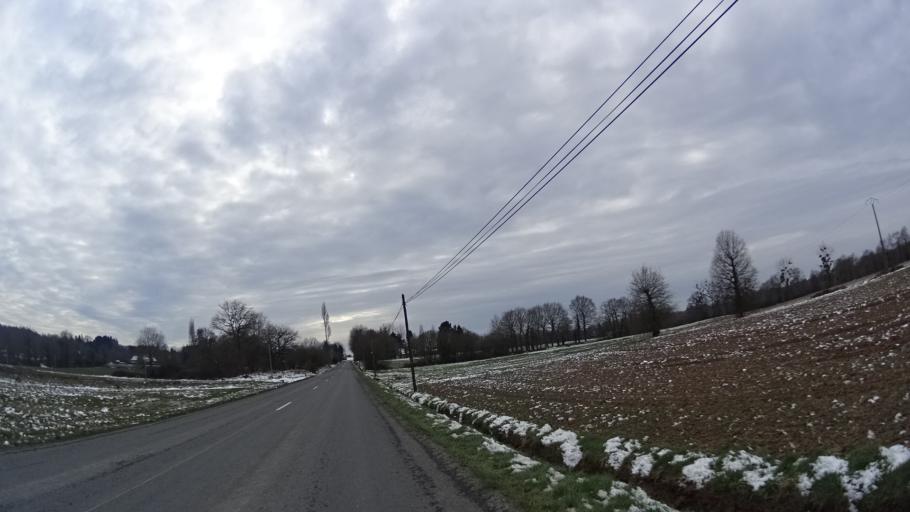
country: FR
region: Brittany
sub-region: Departement d'Ille-et-Vilaine
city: Montauban-de-Bretagne
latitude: 48.2145
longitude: -2.0321
